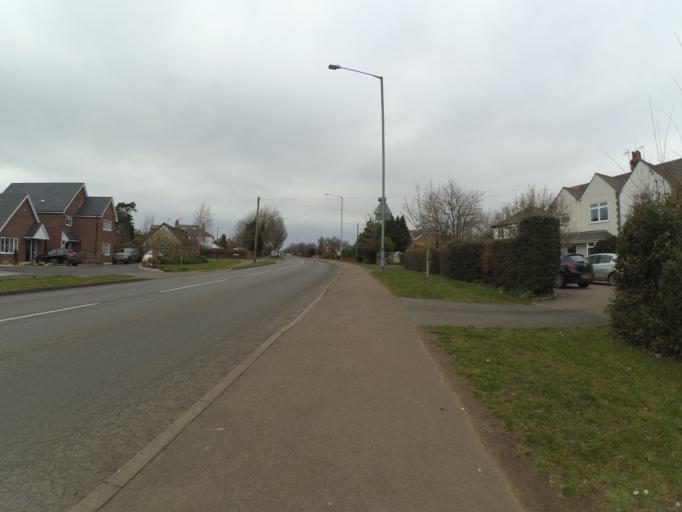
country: GB
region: England
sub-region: Warwickshire
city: Rugby
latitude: 52.3574
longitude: -1.2076
